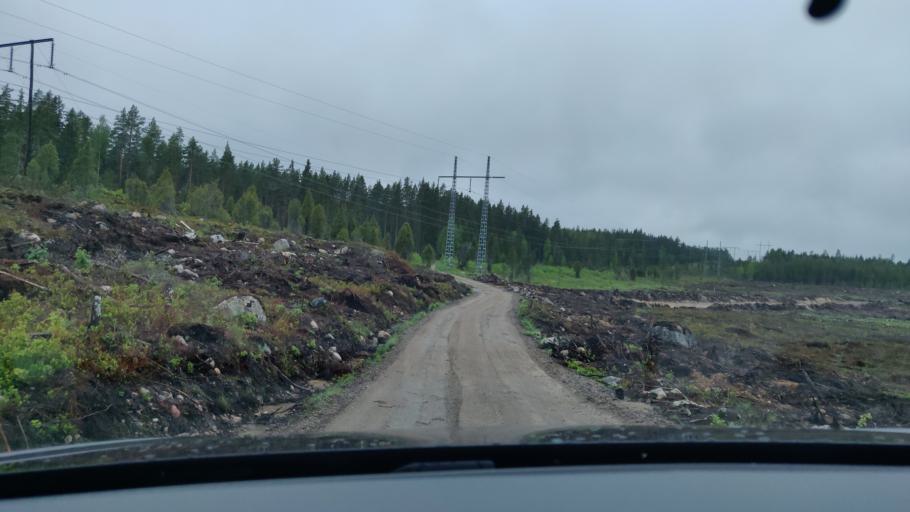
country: SE
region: Dalarna
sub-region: Avesta Kommun
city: Horndal
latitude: 60.3161
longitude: 16.3991
